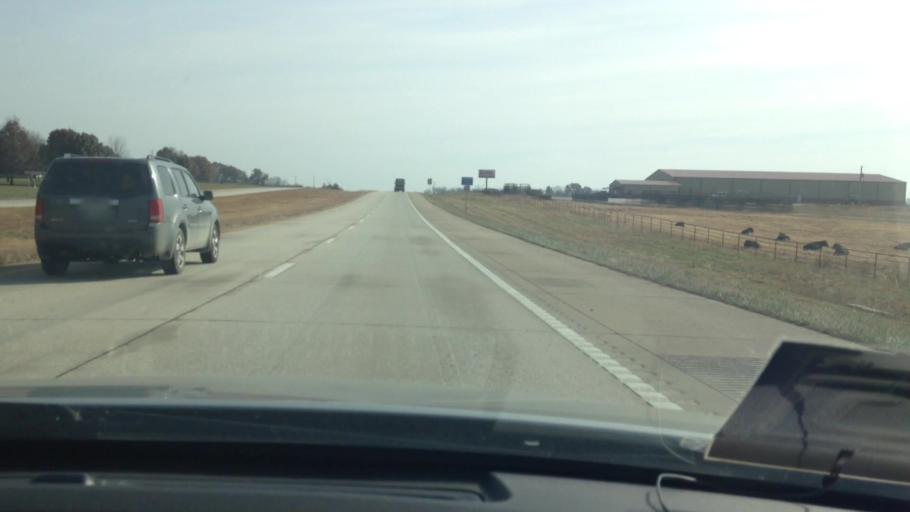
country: US
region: Missouri
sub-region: Henry County
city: Clinton
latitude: 38.4164
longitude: -93.8631
